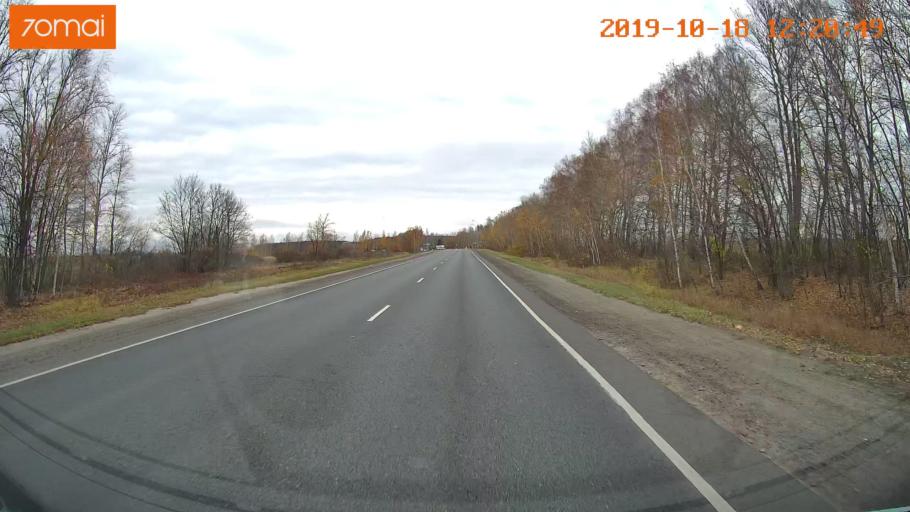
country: RU
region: Rjazan
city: Bagramovo
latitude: 54.5035
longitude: 39.4848
